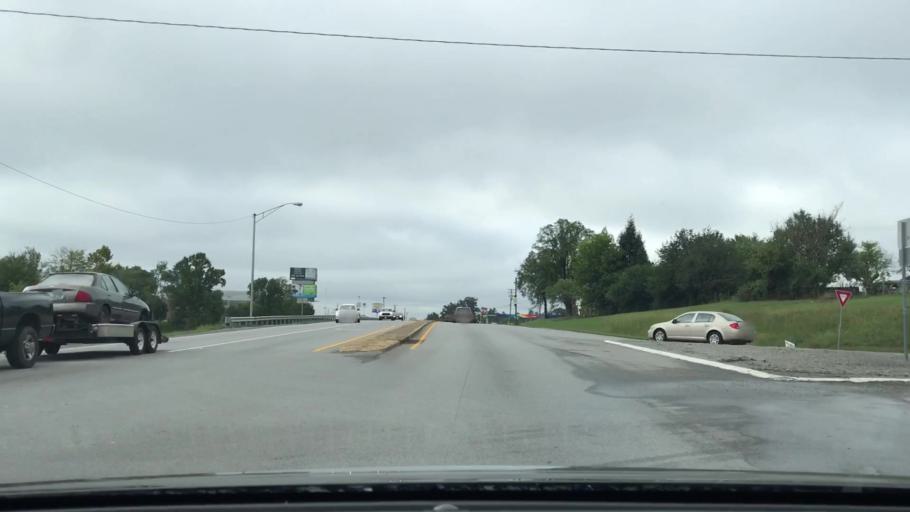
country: US
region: Kentucky
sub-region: Russell County
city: Russell Springs
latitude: 37.0385
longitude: -85.0746
